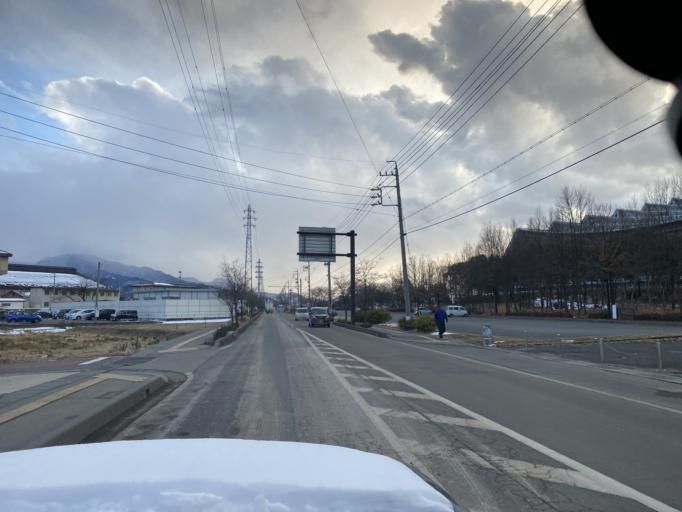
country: JP
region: Nagano
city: Nagano-shi
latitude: 36.6411
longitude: 138.2430
